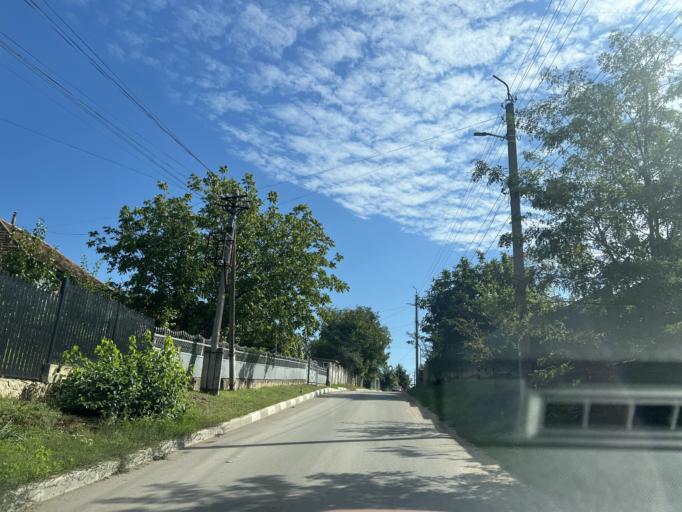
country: MD
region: Ungheni
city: Ungheni
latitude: 47.2004
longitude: 27.8120
